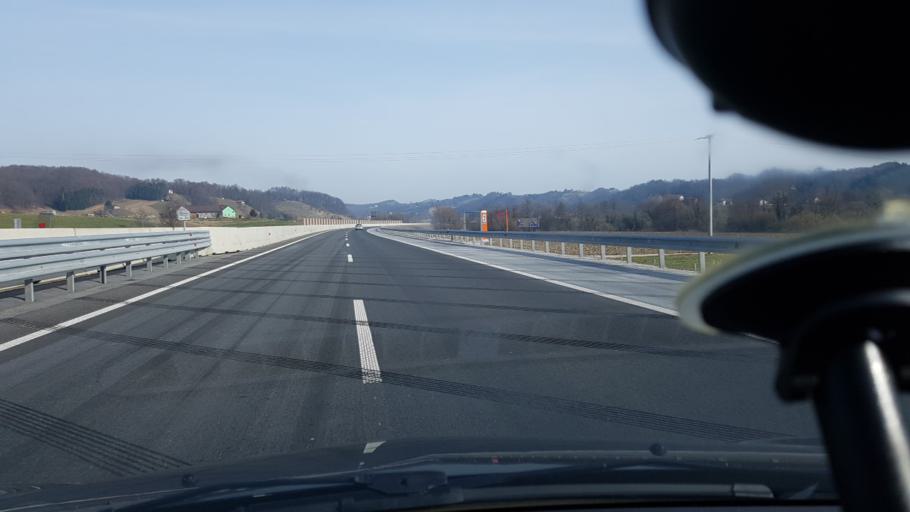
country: SI
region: Podlehnik
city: Podlehnik
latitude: 46.3113
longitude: 15.8675
